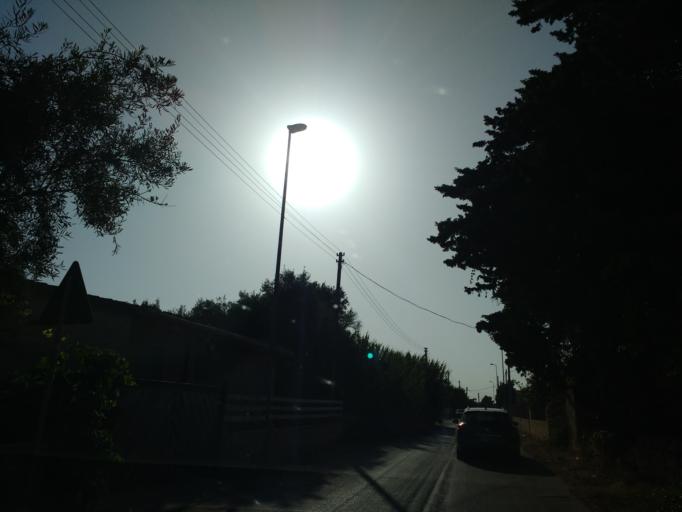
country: IT
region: Sicily
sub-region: Ragusa
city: Cava d'Aliga
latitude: 36.7440
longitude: 14.6741
